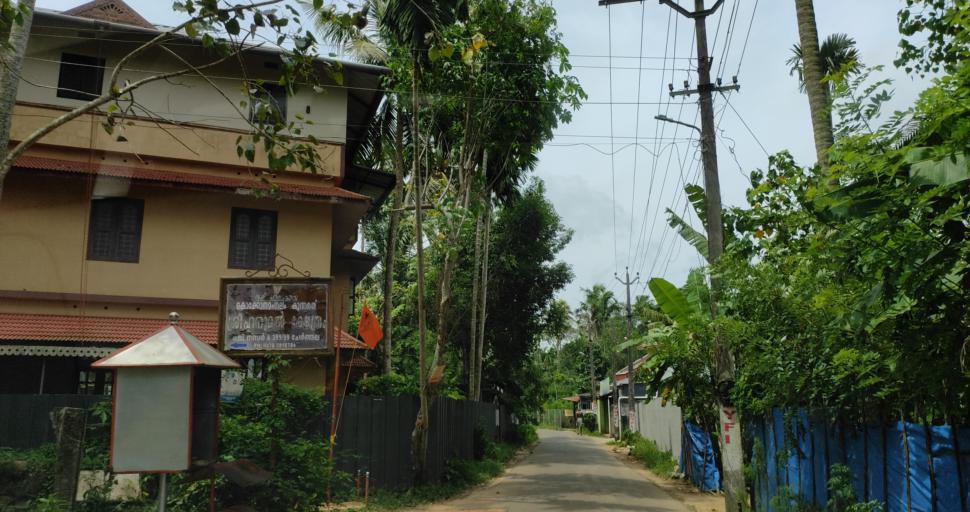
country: IN
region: Kerala
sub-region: Alappuzha
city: Shertallai
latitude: 9.6794
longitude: 76.3583
